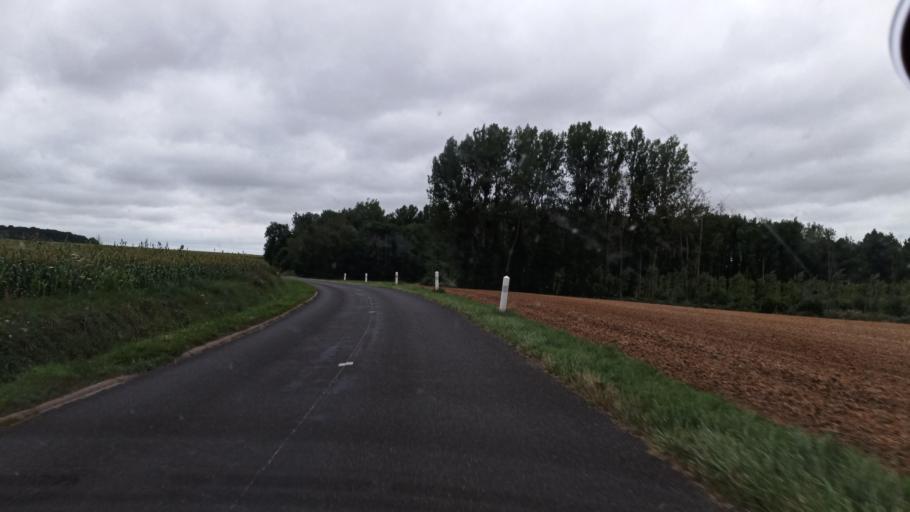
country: FR
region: Ile-de-France
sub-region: Departement de Seine-et-Marne
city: Voulx
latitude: 48.2586
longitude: 3.0164
